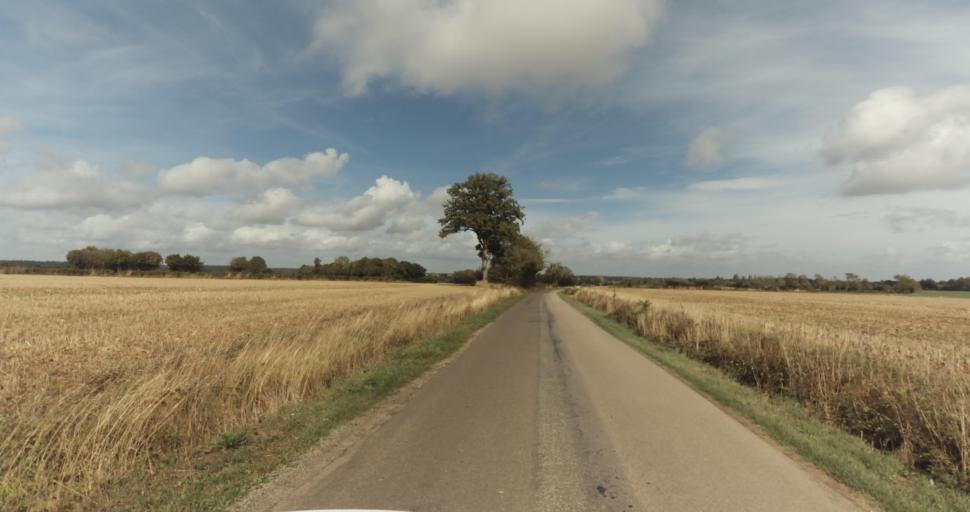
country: FR
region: Lower Normandy
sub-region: Departement de l'Orne
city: Gace
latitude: 48.8168
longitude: 0.3847
